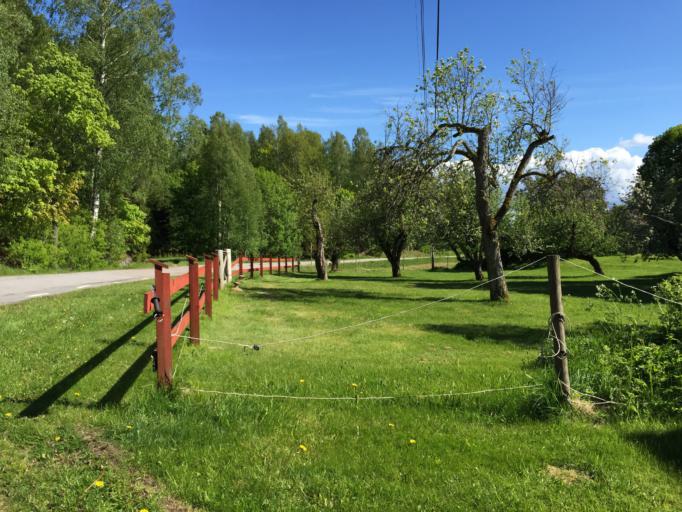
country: SE
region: Soedermanland
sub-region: Vingakers Kommun
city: Vingaker
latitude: 58.9381
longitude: 15.6705
